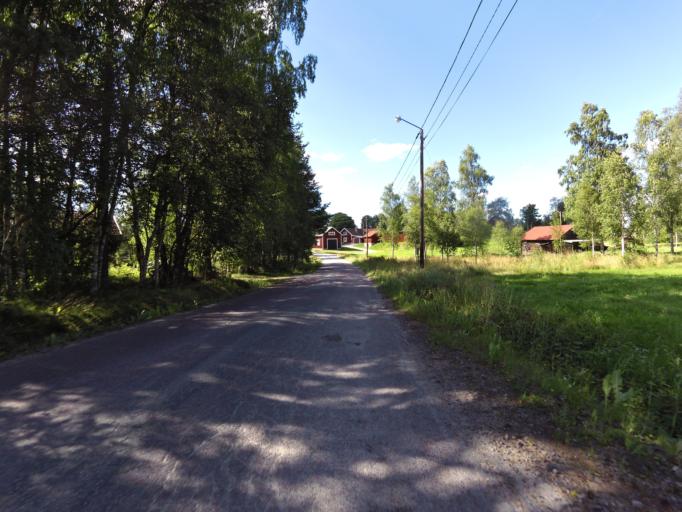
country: SE
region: Dalarna
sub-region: Faluns Kommun
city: Svardsjo
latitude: 60.6385
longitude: 15.8575
